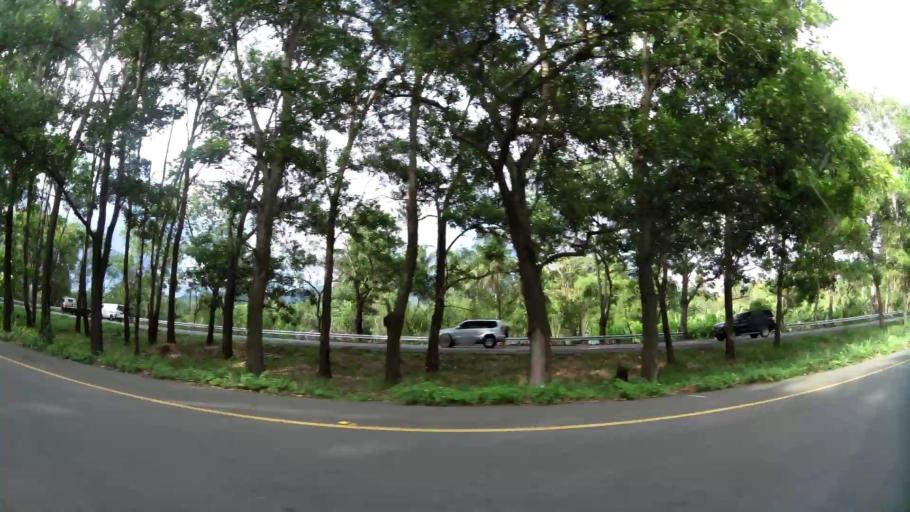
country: DO
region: Monsenor Nouel
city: Piedra Blanca
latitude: 18.8600
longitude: -70.3477
